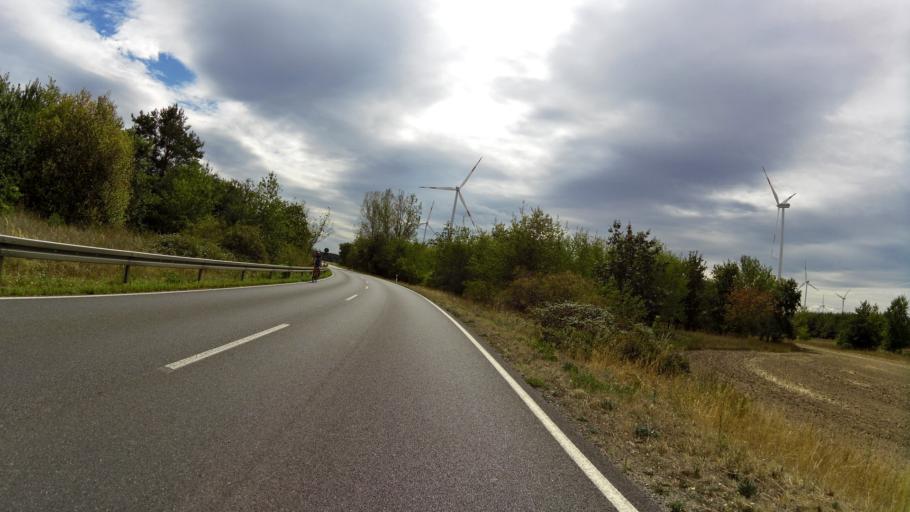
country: DE
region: Brandenburg
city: Heinersbruck
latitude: 51.7853
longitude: 14.4725
